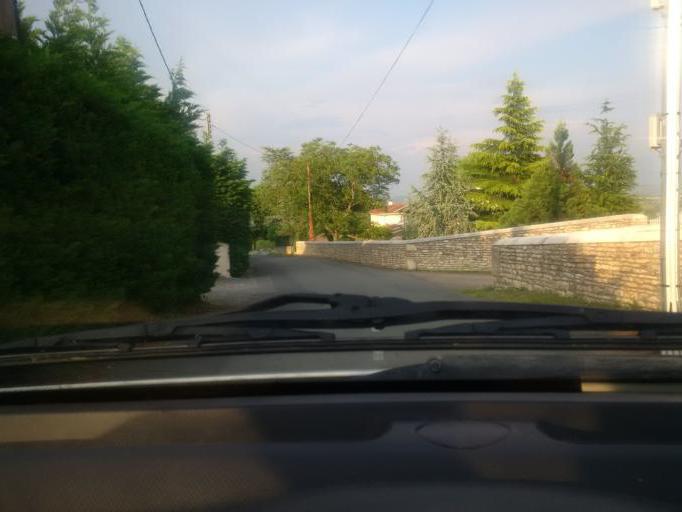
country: FR
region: Rhone-Alpes
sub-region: Departement du Rhone
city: Lucenay
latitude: 45.9158
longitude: 4.6987
